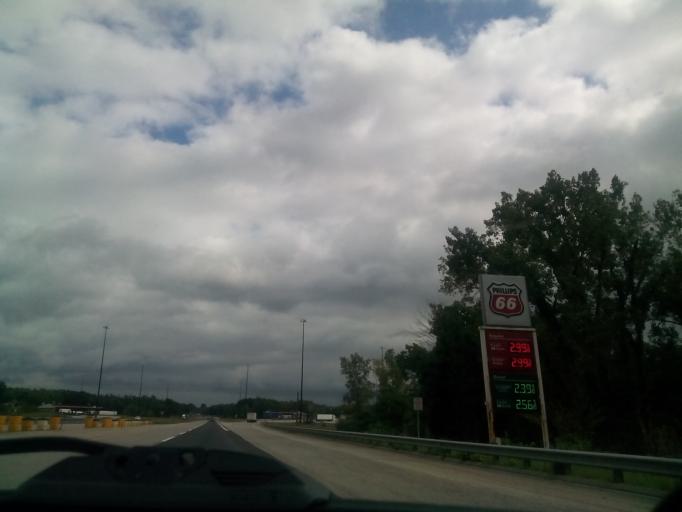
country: US
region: Indiana
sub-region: Steuben County
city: Fremont
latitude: 41.7292
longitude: -84.9701
